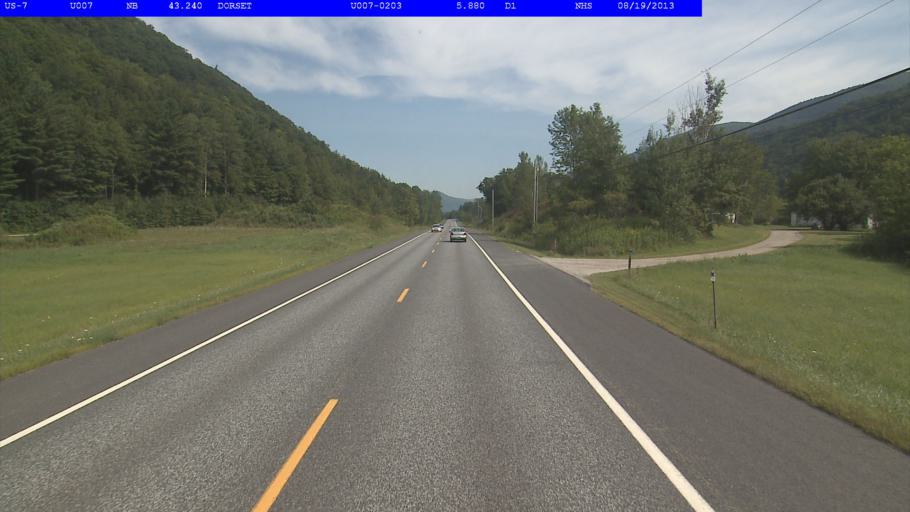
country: US
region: Vermont
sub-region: Bennington County
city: Manchester Center
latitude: 43.2932
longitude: -72.9986
